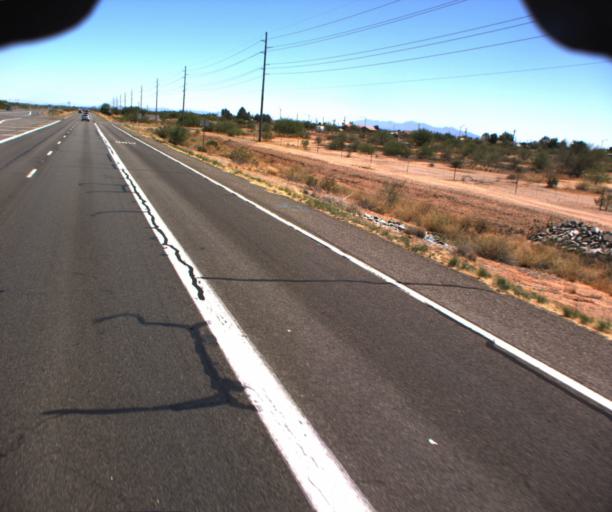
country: US
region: Arizona
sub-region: Maricopa County
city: Sun City West
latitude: 33.7146
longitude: -112.4477
